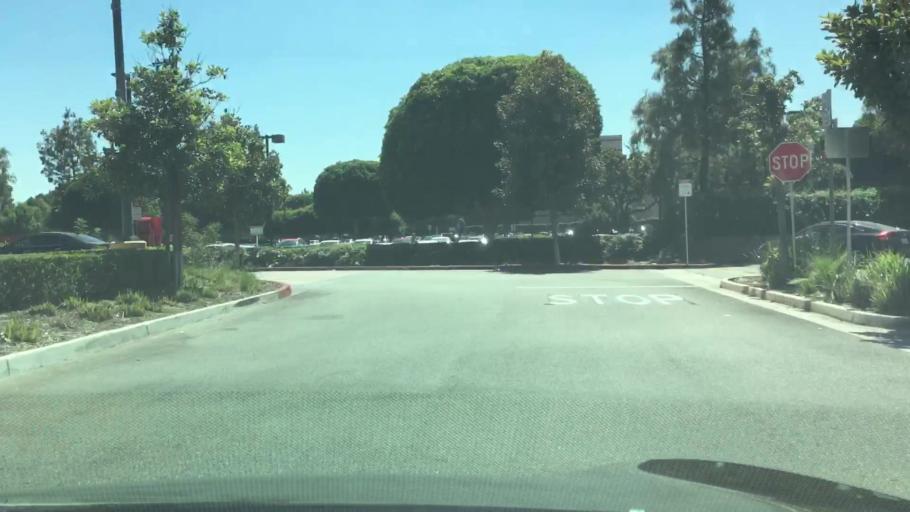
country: US
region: California
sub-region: Los Angeles County
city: South San Gabriel
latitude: 34.0496
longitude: -118.0828
